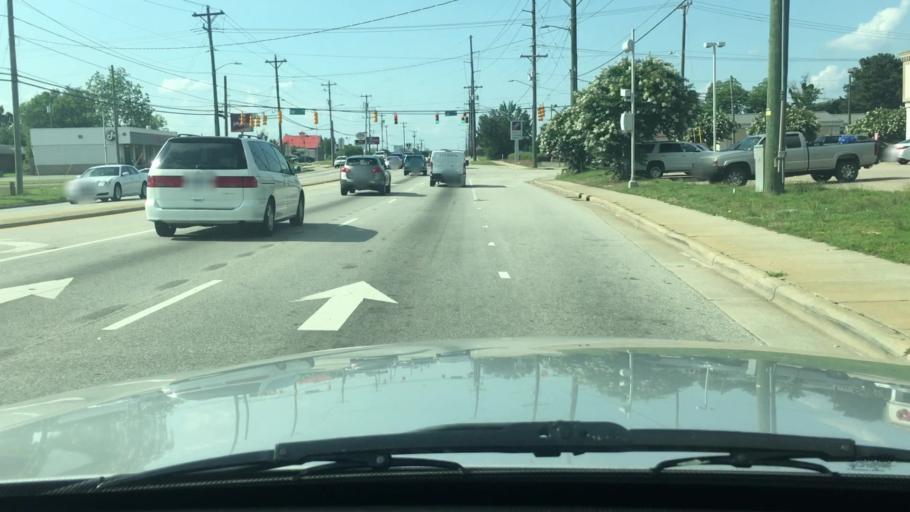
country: US
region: North Carolina
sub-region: Cumberland County
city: Fayetteville
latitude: 35.1070
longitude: -78.8786
